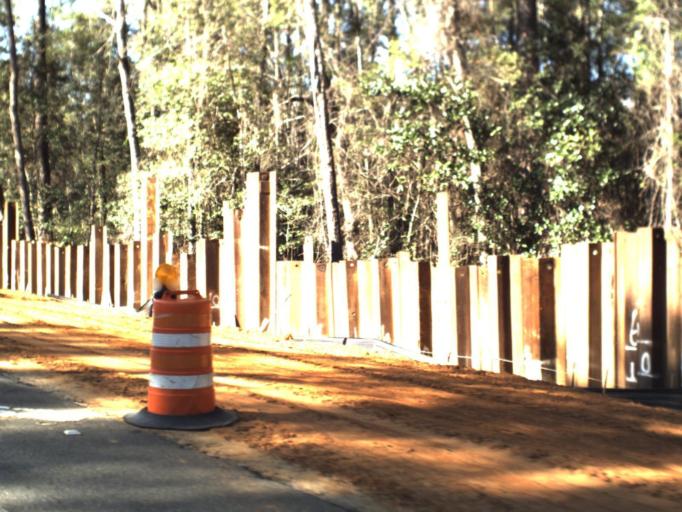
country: US
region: Florida
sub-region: Calhoun County
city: Blountstown
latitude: 30.4291
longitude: -85.1689
